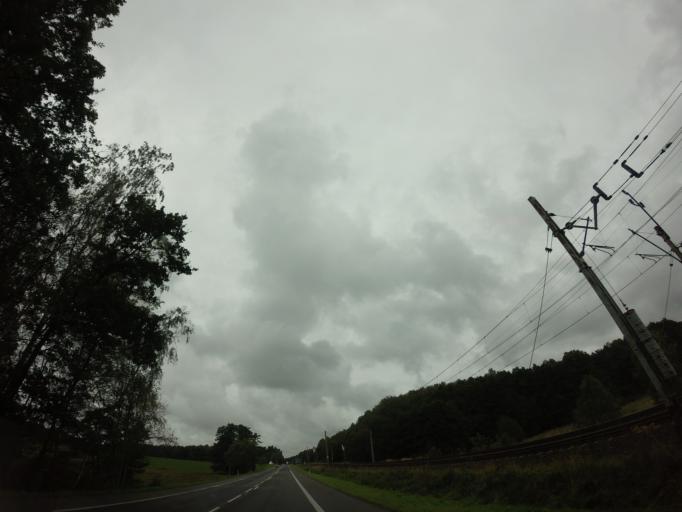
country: PL
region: West Pomeranian Voivodeship
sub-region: Powiat kamienski
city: Wolin
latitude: 53.8445
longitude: 14.7032
